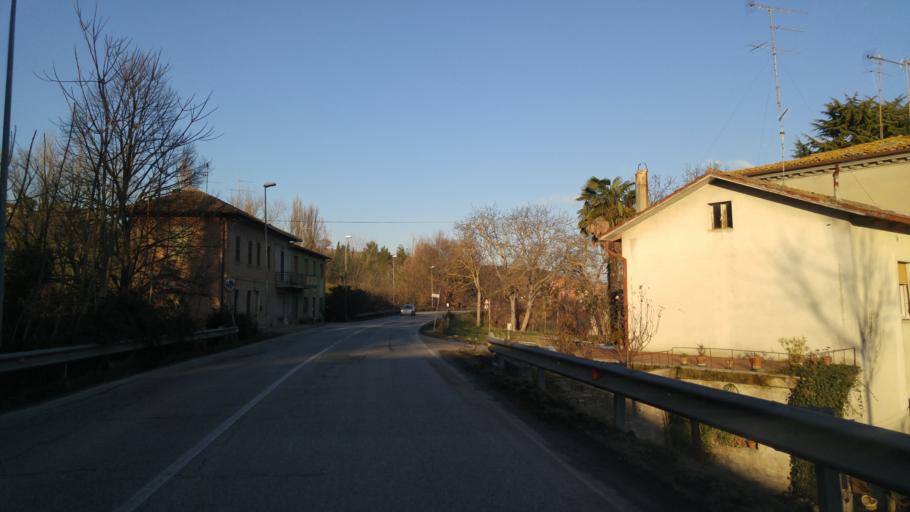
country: IT
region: The Marches
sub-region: Provincia di Pesaro e Urbino
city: San Michele
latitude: 43.6766
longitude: 13.0216
